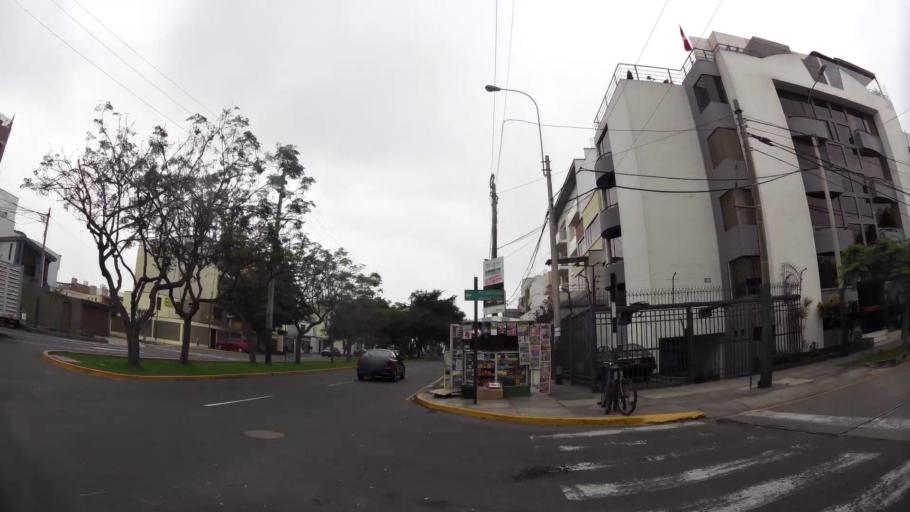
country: PE
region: Lima
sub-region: Lima
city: Surco
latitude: -12.1364
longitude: -76.9906
